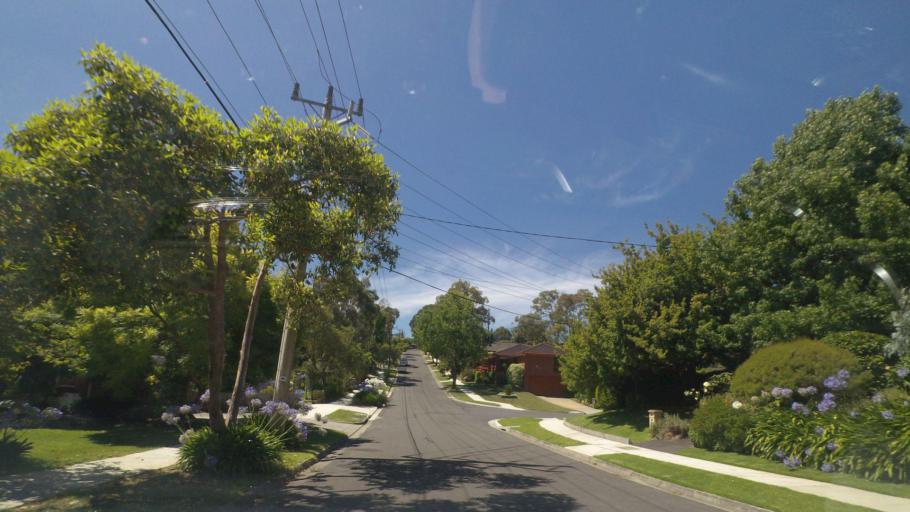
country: AU
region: Victoria
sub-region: Manningham
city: Park Orchards
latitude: -37.7947
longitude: 145.2257
